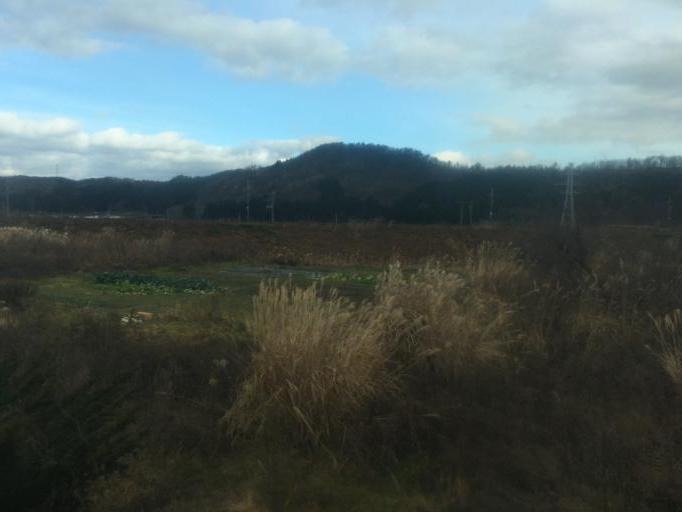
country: JP
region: Akita
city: Takanosu
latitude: 40.2025
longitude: 140.2112
